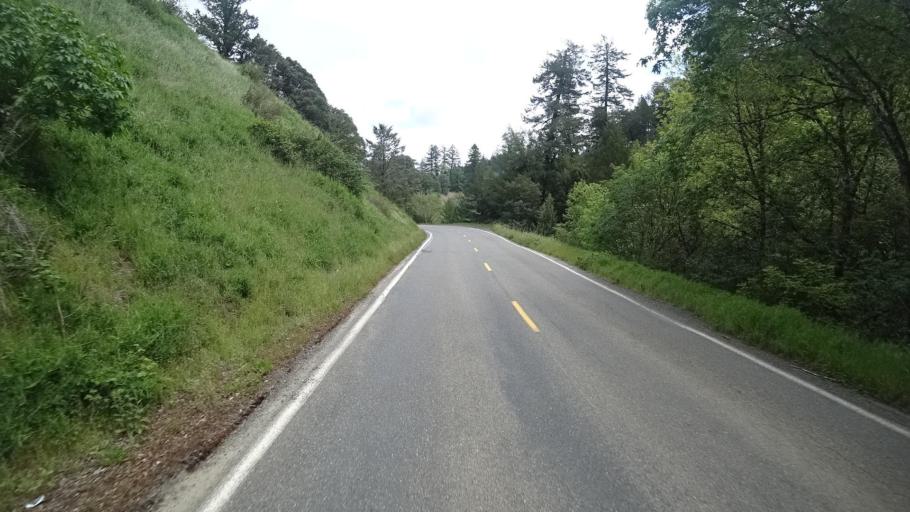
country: US
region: California
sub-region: Humboldt County
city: Redway
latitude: 40.1253
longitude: -123.8718
